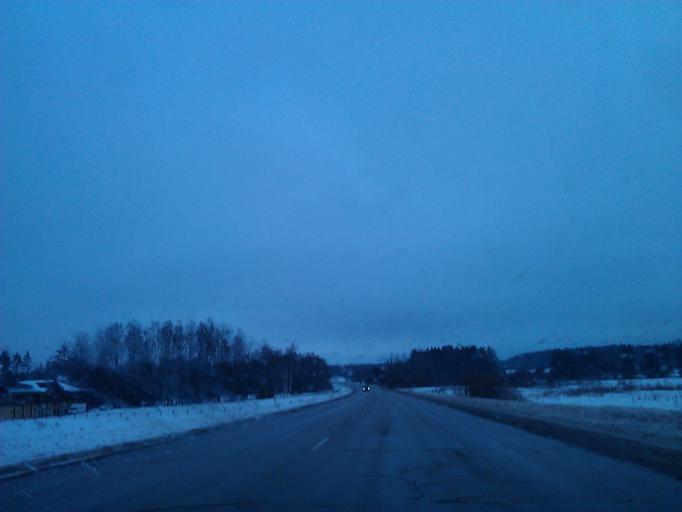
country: LV
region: Cesu Rajons
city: Cesis
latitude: 57.2863
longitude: 25.2974
